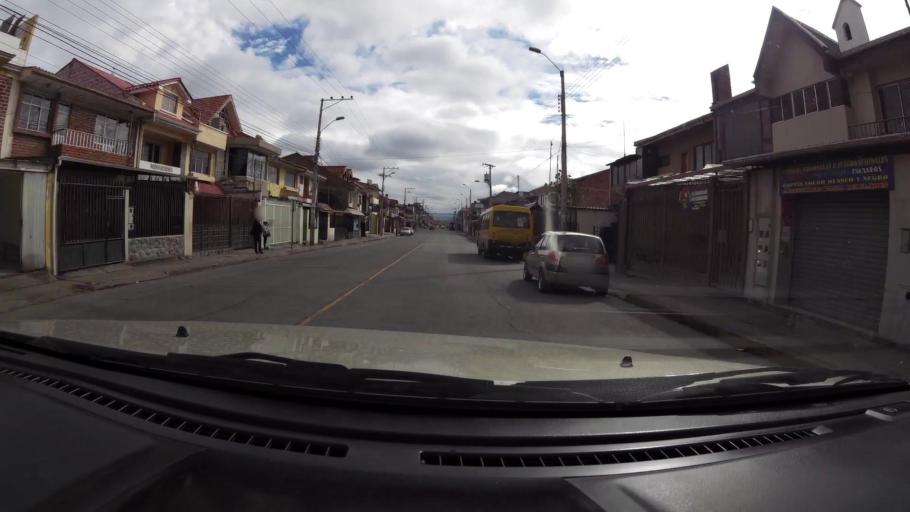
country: EC
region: Azuay
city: Cuenca
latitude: -2.8953
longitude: -78.9818
